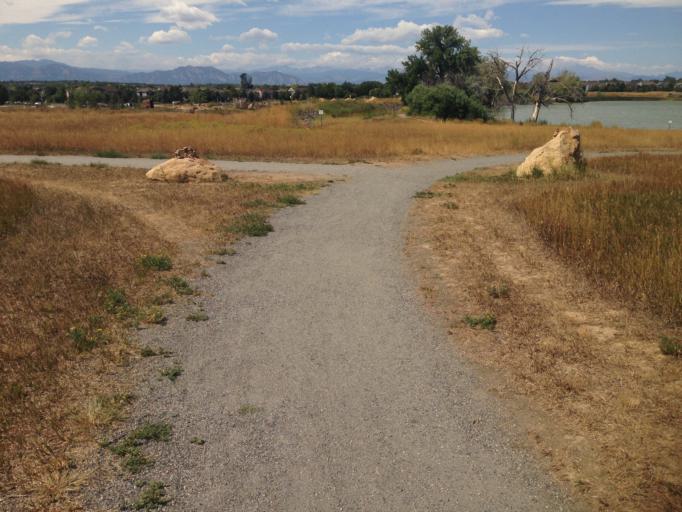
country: US
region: Colorado
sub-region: Adams County
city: Northglenn
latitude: 39.9501
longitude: -105.0115
